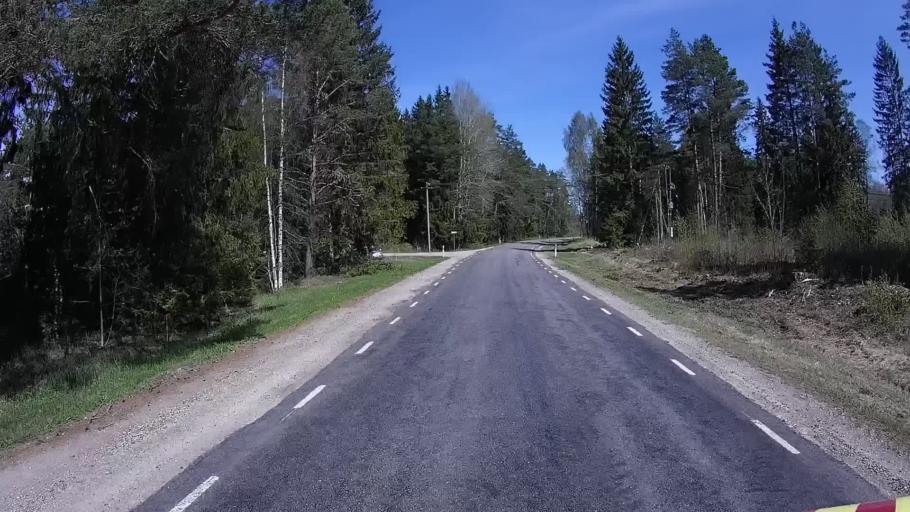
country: EE
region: Harju
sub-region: Nissi vald
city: Turba
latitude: 59.0978
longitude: 24.0020
